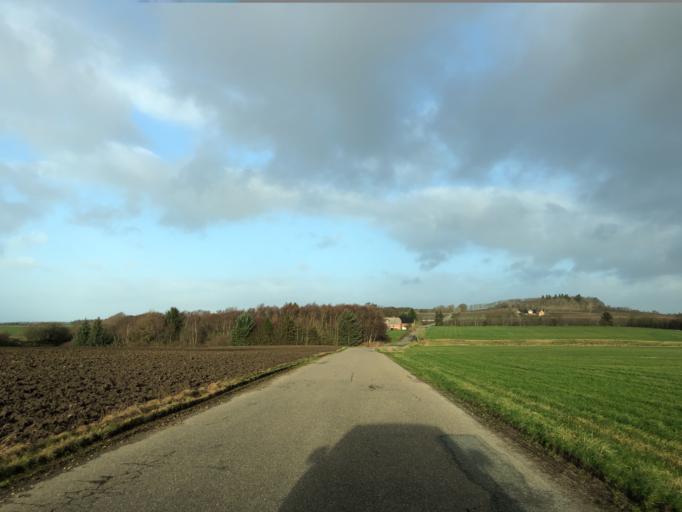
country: DK
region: Central Jutland
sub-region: Ringkobing-Skjern Kommune
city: Videbaek
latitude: 56.1801
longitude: 8.5391
